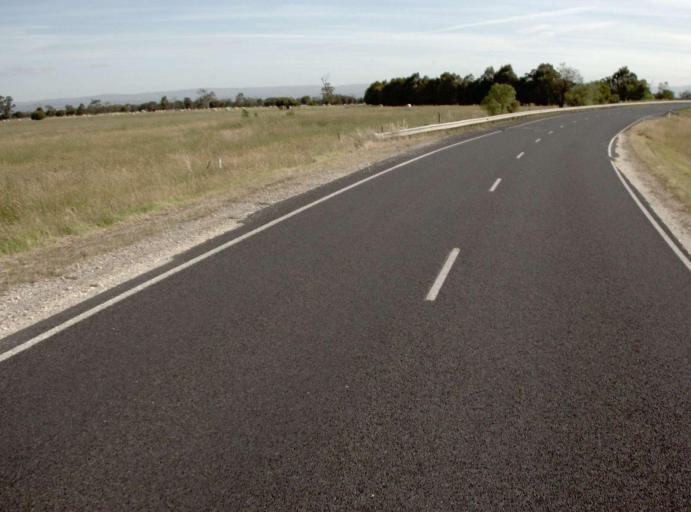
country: AU
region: Victoria
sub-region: Latrobe
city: Traralgon
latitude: -38.1045
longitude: 146.5931
